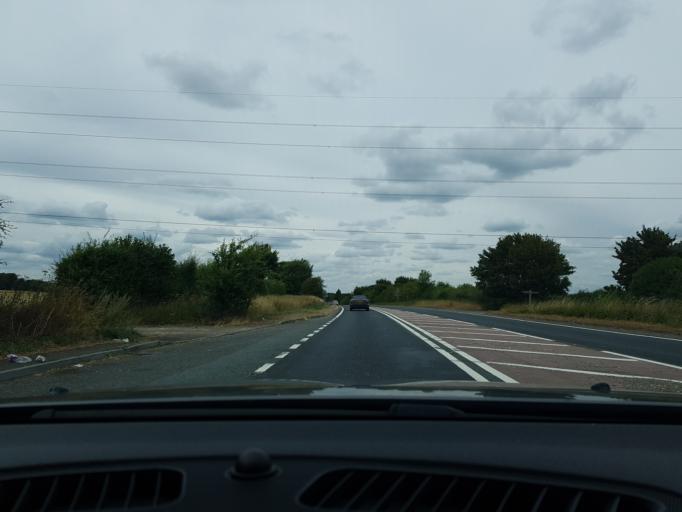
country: GB
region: England
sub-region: Hampshire
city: Kingsclere
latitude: 51.3113
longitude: -1.1997
